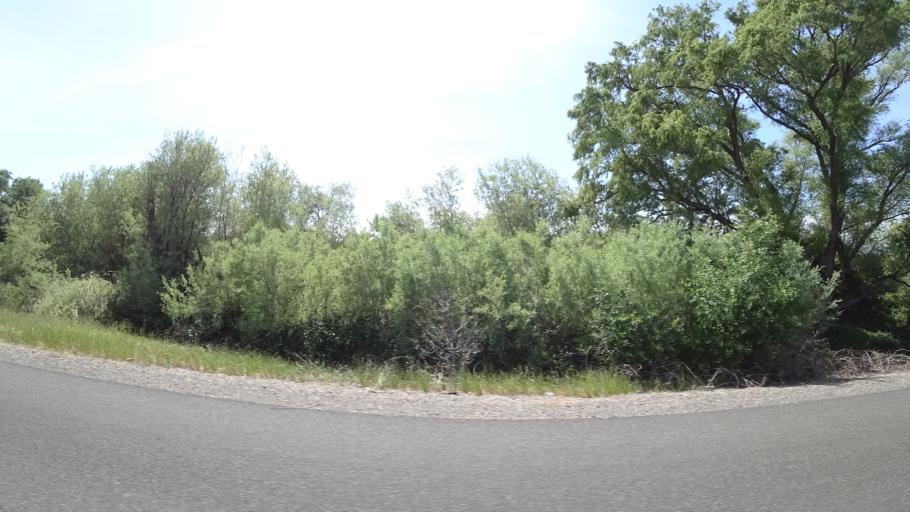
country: US
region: California
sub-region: Shasta County
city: Redding
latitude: 40.5277
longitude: -122.3479
